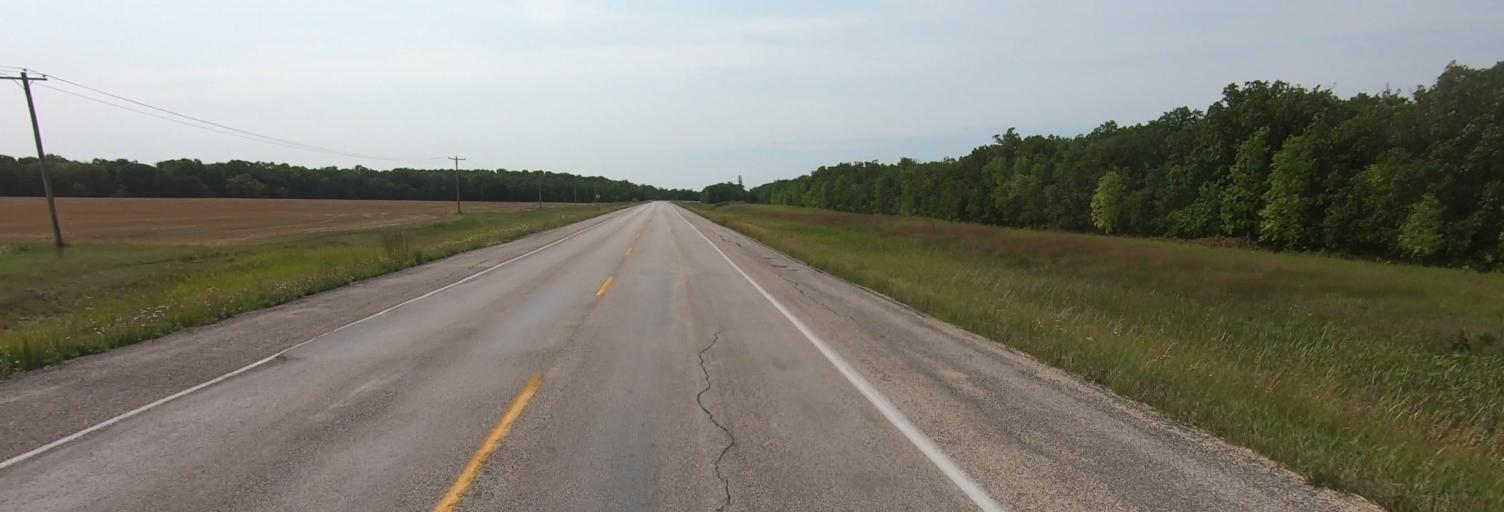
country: CA
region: Manitoba
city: Niverville
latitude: 49.5952
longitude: -97.1347
